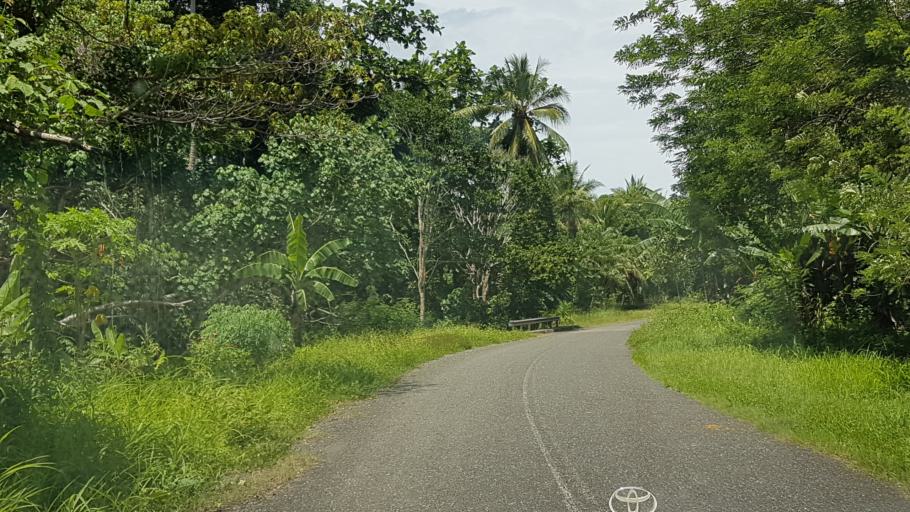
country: PG
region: Madang
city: Madang
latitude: -4.5158
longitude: 145.4644
